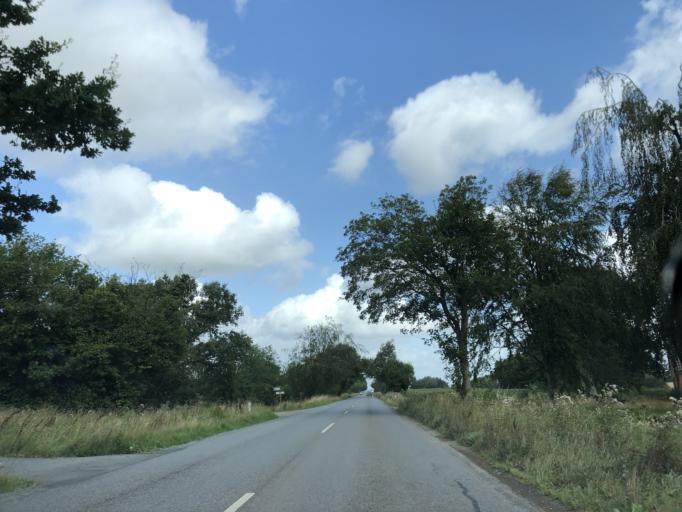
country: DK
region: South Denmark
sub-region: Haderslev Kommune
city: Haderslev
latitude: 55.2194
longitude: 9.5008
